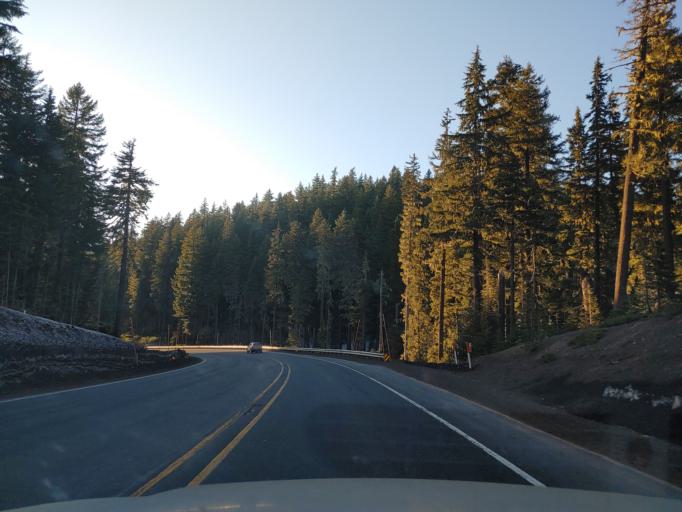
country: US
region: Oregon
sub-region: Lane County
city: Oakridge
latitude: 43.6110
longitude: -122.0595
